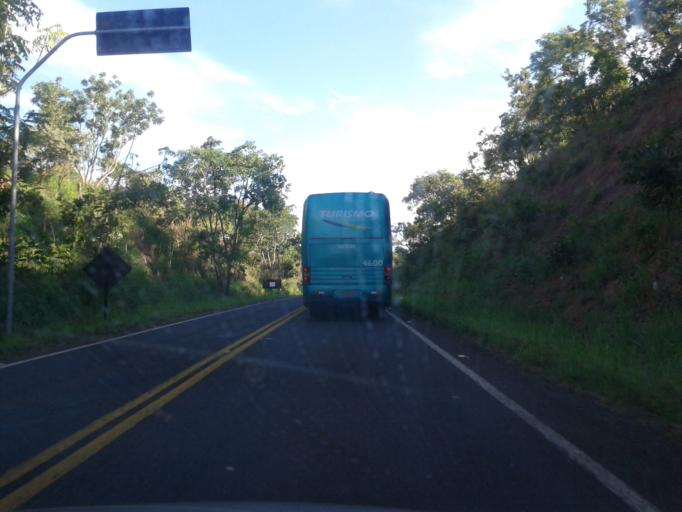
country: BR
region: Minas Gerais
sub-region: Tupaciguara
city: Tupaciguara
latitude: -18.3114
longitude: -48.5617
